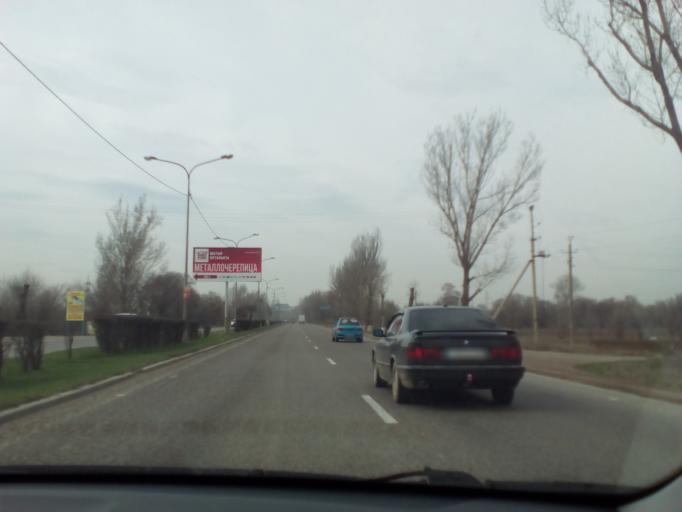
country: KZ
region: Almaty Oblysy
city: Burunday
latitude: 43.2218
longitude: 76.6217
